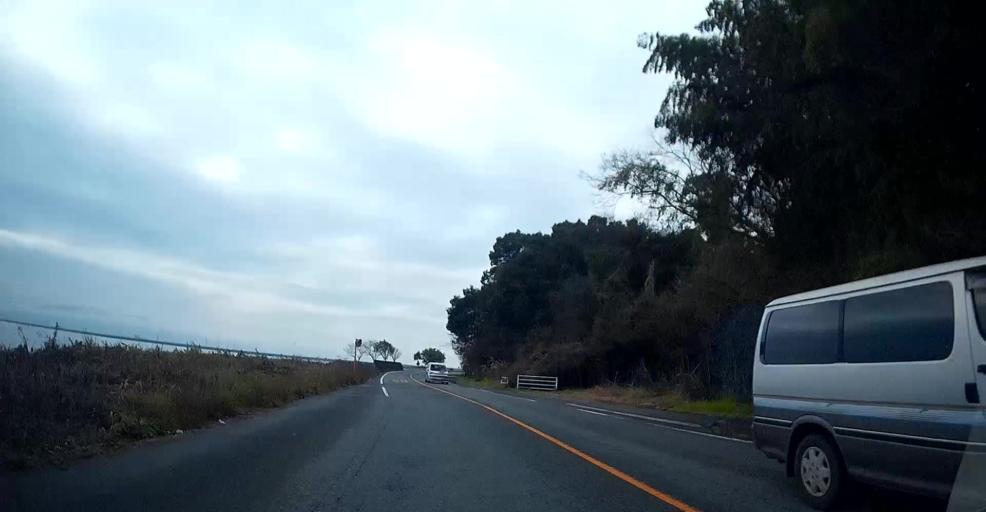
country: JP
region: Kumamoto
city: Matsubase
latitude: 32.6347
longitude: 130.6363
